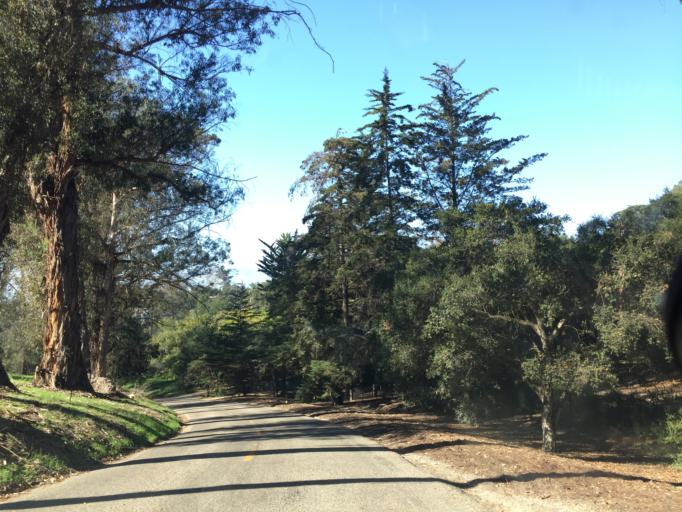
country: US
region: California
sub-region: Santa Barbara County
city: Goleta
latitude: 34.4290
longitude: -119.7749
